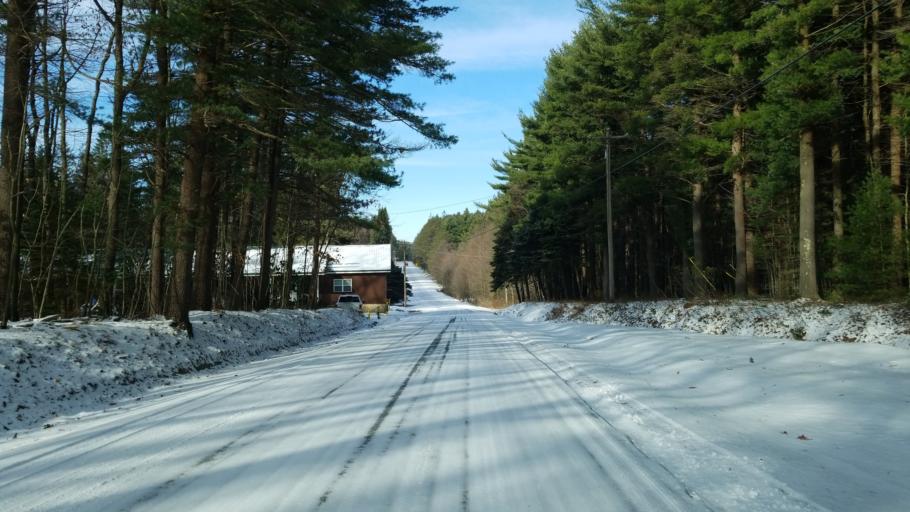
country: US
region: Pennsylvania
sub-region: Clearfield County
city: Clearfield
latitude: 41.1180
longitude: -78.5294
